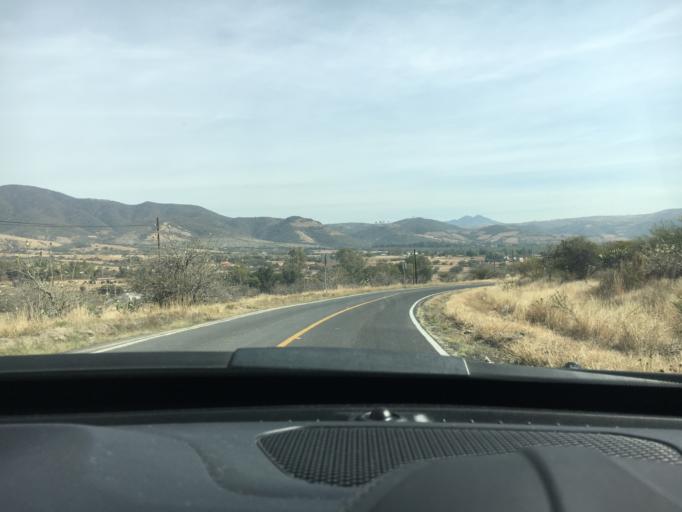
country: MX
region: Guanajuato
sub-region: Silao de la Victoria
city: San Francisco (Banos de Agua Caliente)
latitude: 21.0738
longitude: -101.4910
